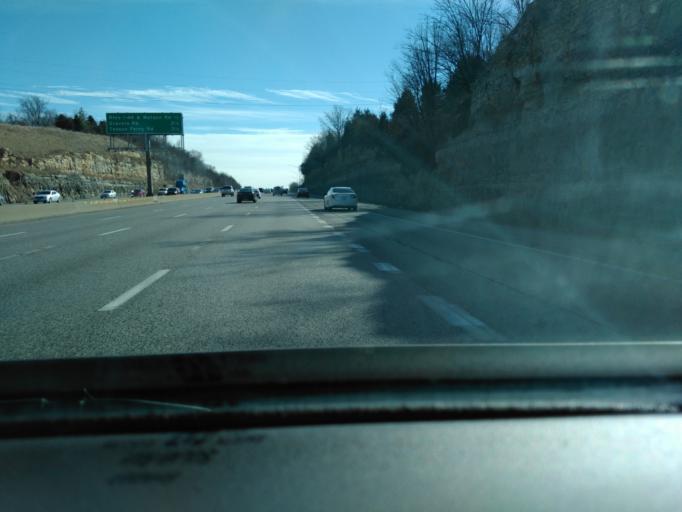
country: US
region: Missouri
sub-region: Saint Louis County
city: Sunset Hills
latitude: 38.5597
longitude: -90.4372
